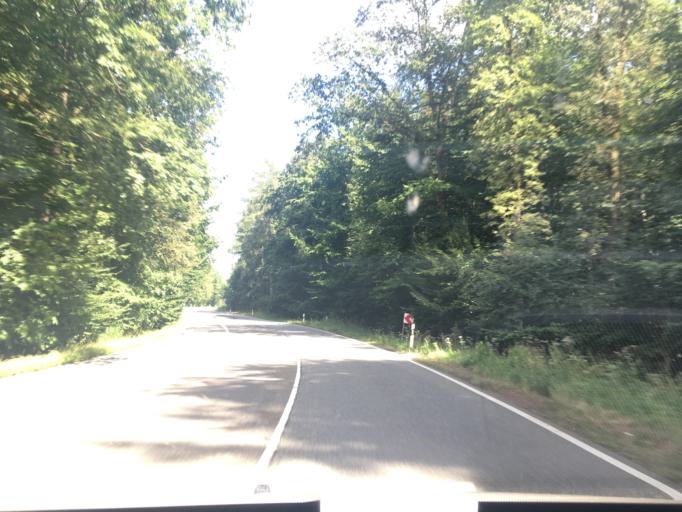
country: DE
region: Saarland
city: Sulzbach
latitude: 49.2751
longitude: 7.0784
